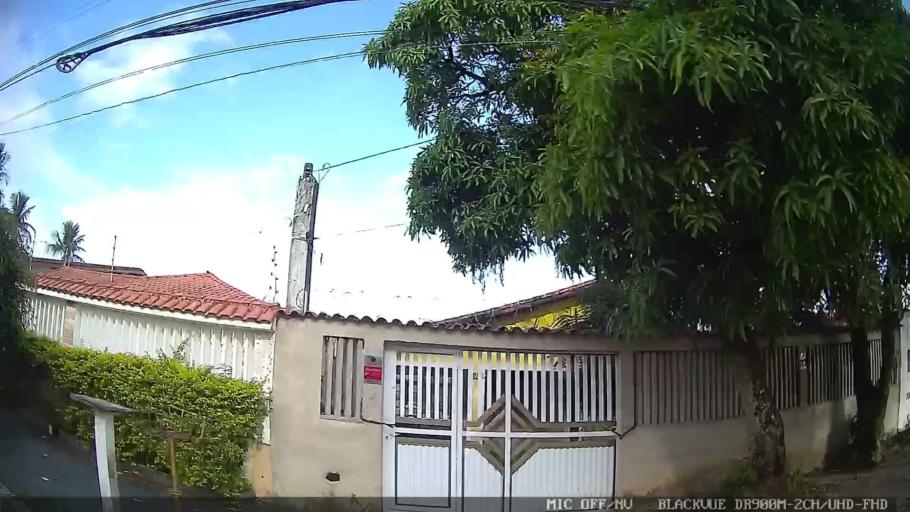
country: BR
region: Sao Paulo
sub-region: Peruibe
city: Peruibe
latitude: -24.3104
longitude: -46.9906
